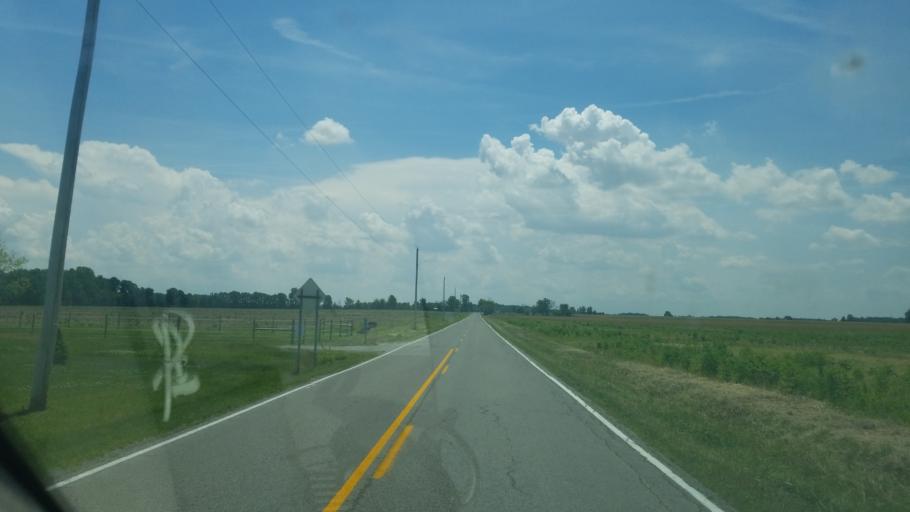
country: US
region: Ohio
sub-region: Hancock County
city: Arlington
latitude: 40.9052
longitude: -83.5947
